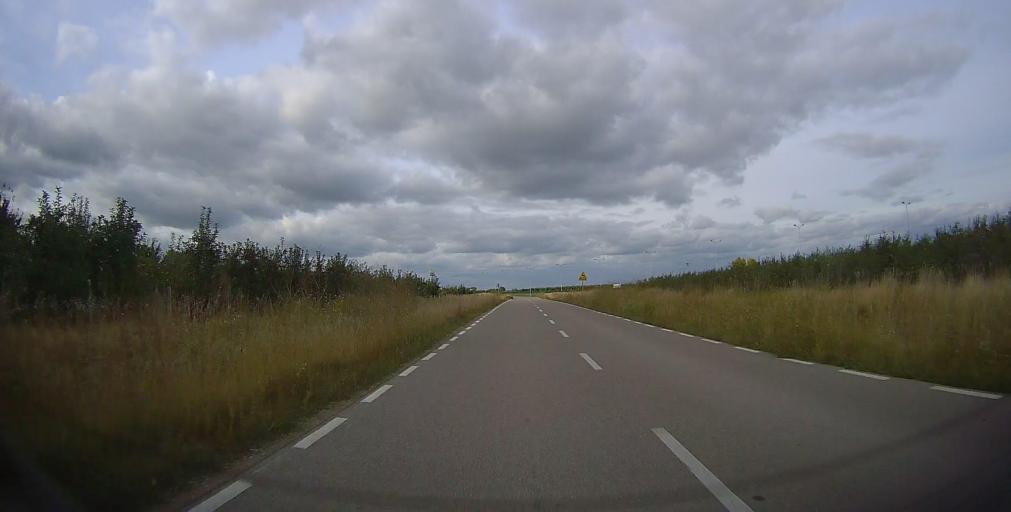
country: PL
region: Masovian Voivodeship
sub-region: Powiat grojecki
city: Goszczyn
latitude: 51.7383
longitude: 20.9121
